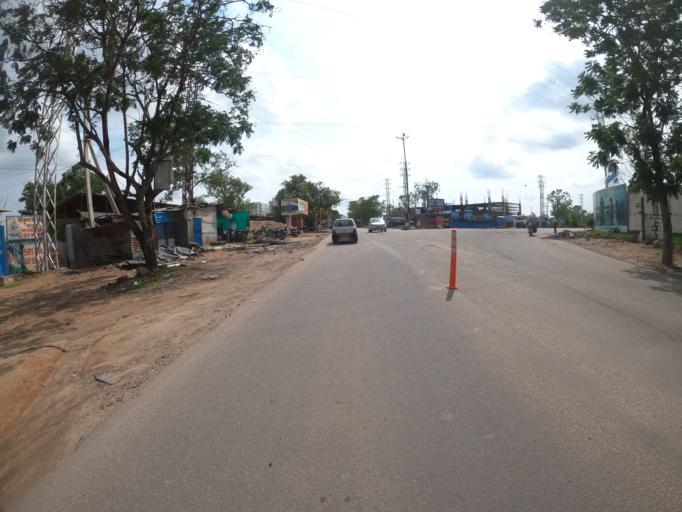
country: IN
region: Telangana
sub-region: Medak
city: Serilingampalle
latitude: 17.3853
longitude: 78.3313
